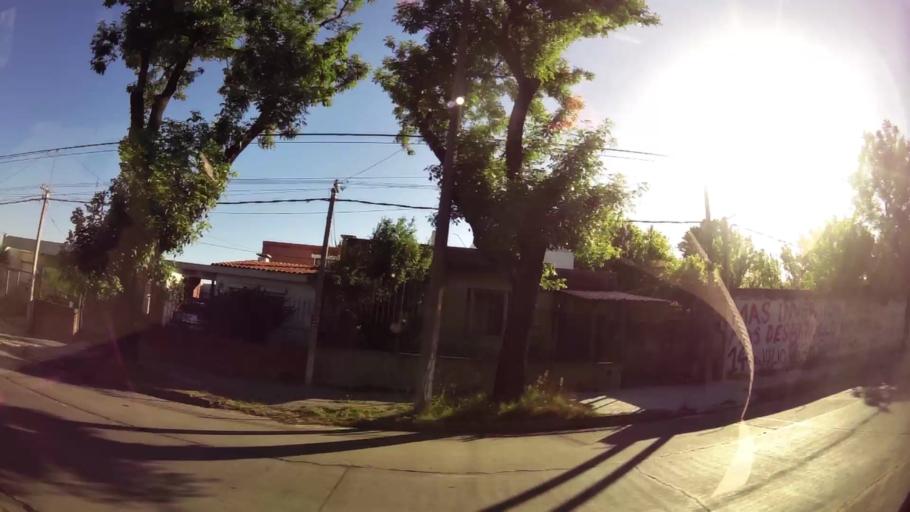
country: UY
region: Montevideo
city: Montevideo
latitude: -34.8386
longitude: -56.2149
